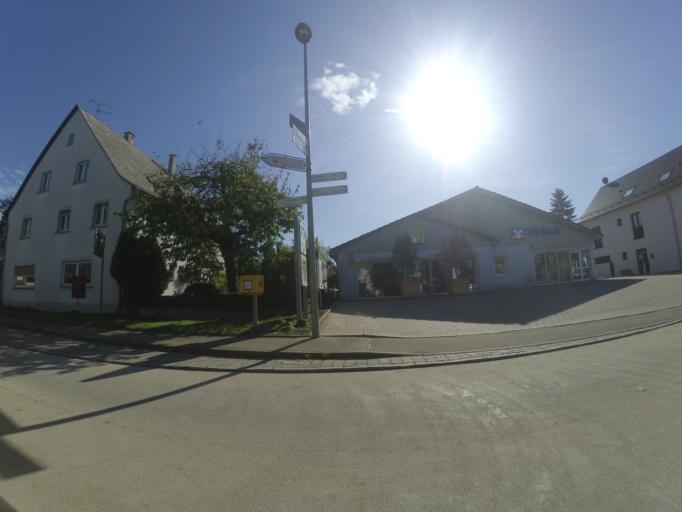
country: DE
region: Baden-Wuerttemberg
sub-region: Tuebingen Region
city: Weidenstetten
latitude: 48.5522
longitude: 9.9973
